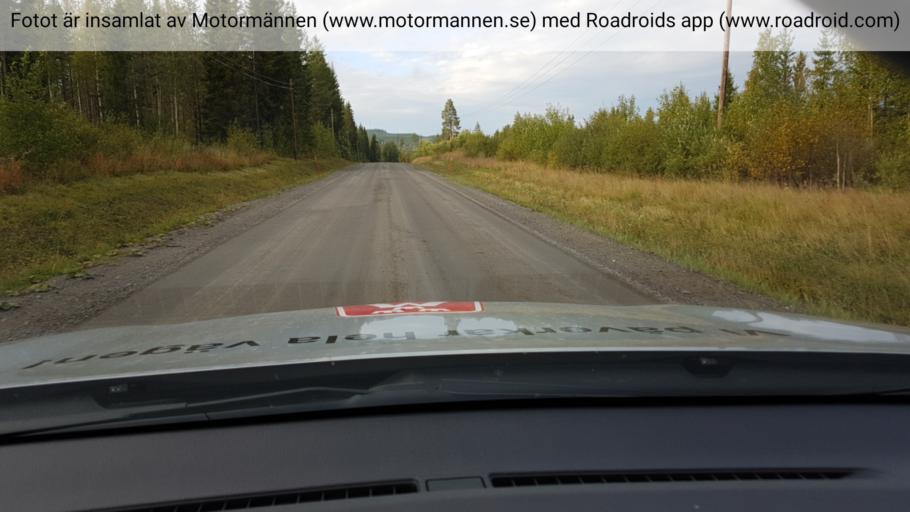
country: SE
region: Jaemtland
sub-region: Stroemsunds Kommun
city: Stroemsund
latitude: 63.9817
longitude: 15.8196
